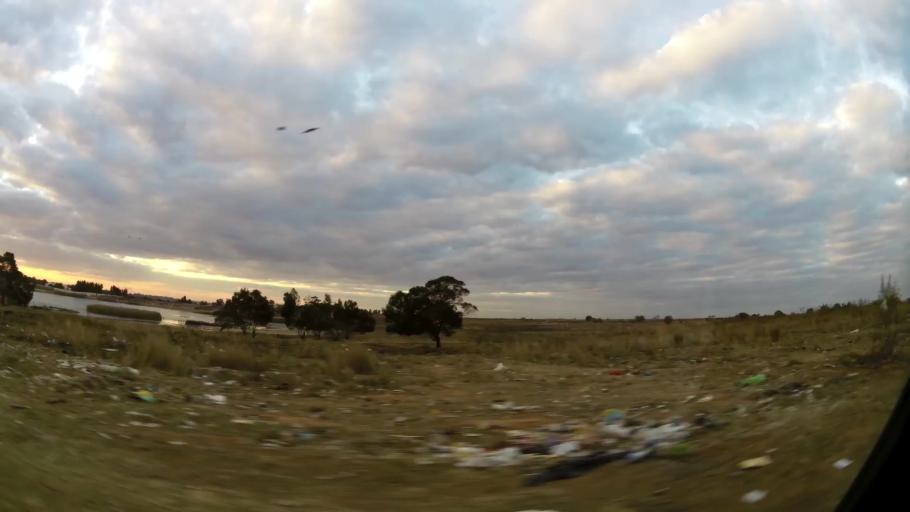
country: ZA
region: Gauteng
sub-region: City of Johannesburg Metropolitan Municipality
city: Midrand
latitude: -25.9794
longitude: 28.1676
